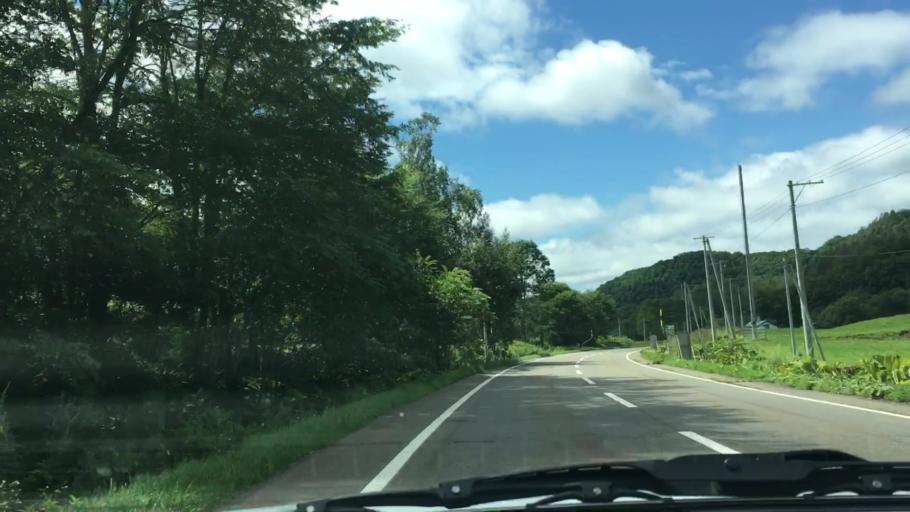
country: JP
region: Hokkaido
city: Kitami
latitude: 43.3710
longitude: 143.8707
